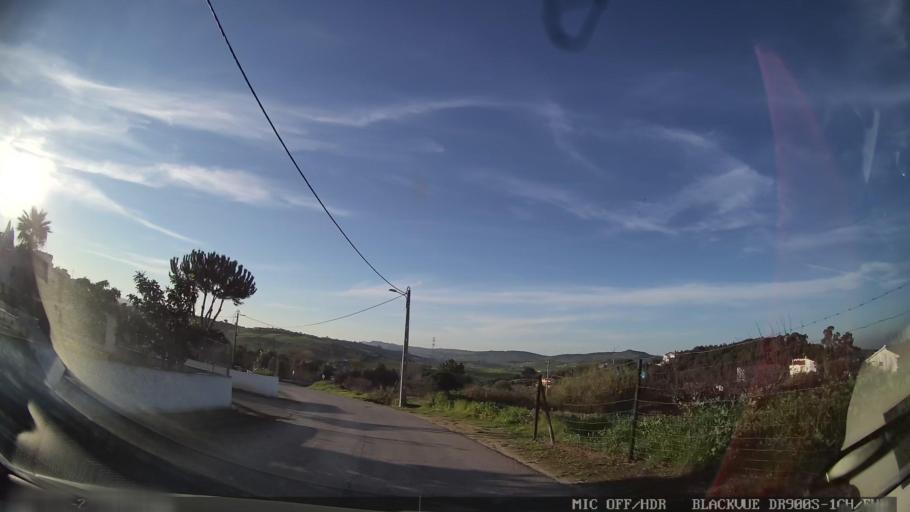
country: PT
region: Lisbon
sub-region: Vila Franca de Xira
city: Vila Franca de Xira
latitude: 38.9876
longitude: -9.0131
